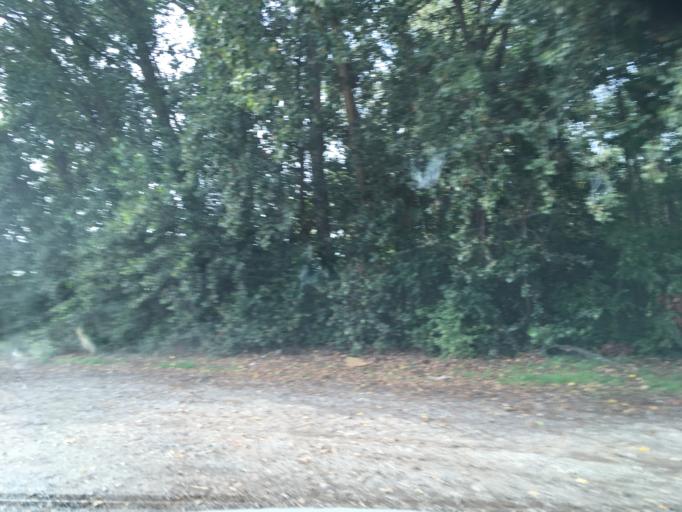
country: DE
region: Baden-Wuerttemberg
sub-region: Freiburg Region
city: Kehl
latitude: 48.6021
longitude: 7.8111
